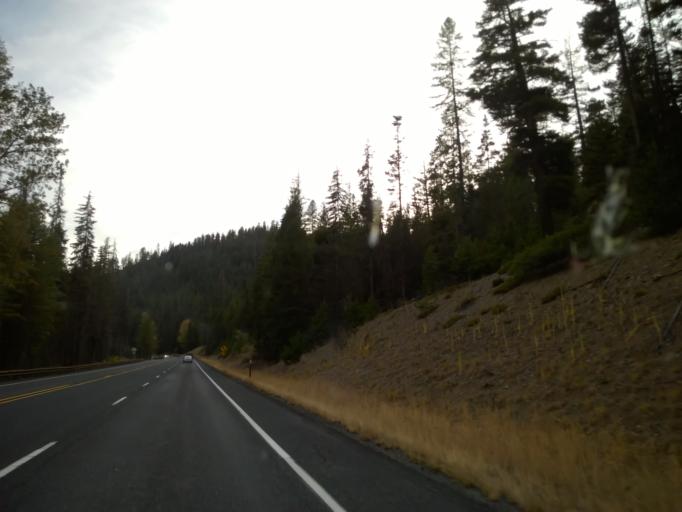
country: US
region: Washington
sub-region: Chelan County
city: Cashmere
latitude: 47.3537
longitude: -120.5673
